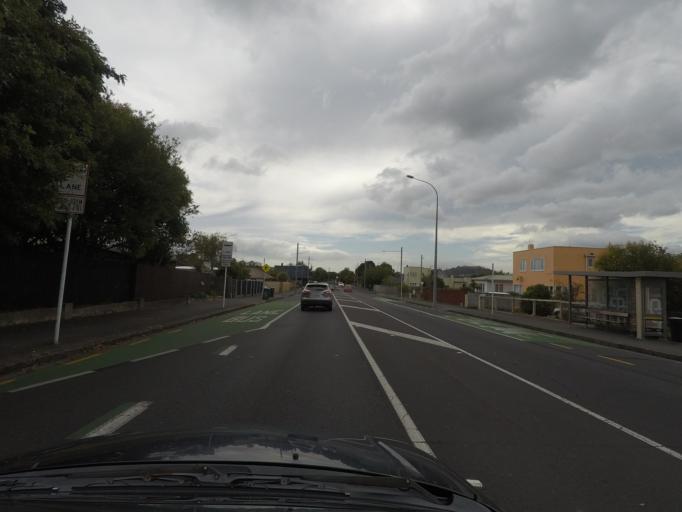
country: NZ
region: Auckland
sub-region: Auckland
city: Auckland
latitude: -36.8942
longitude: 174.7356
